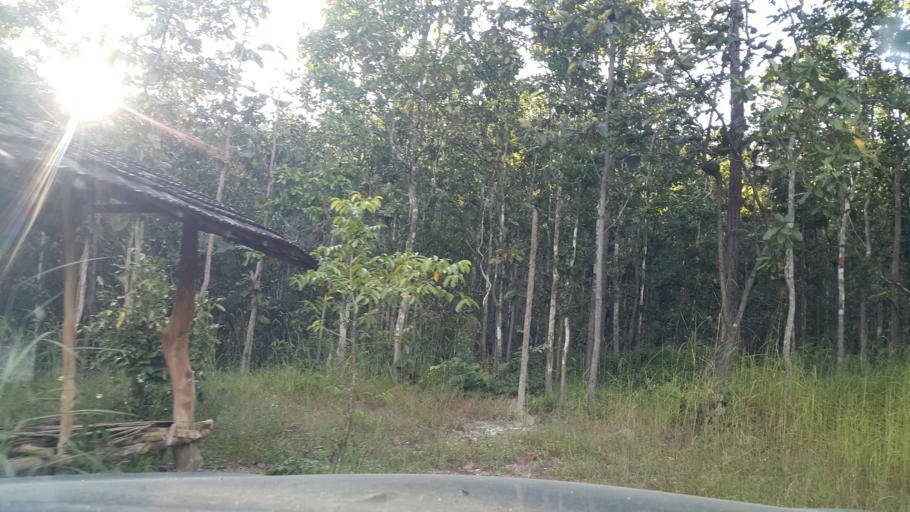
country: TH
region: Chiang Mai
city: San Kamphaeng
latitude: 18.7057
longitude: 99.1922
